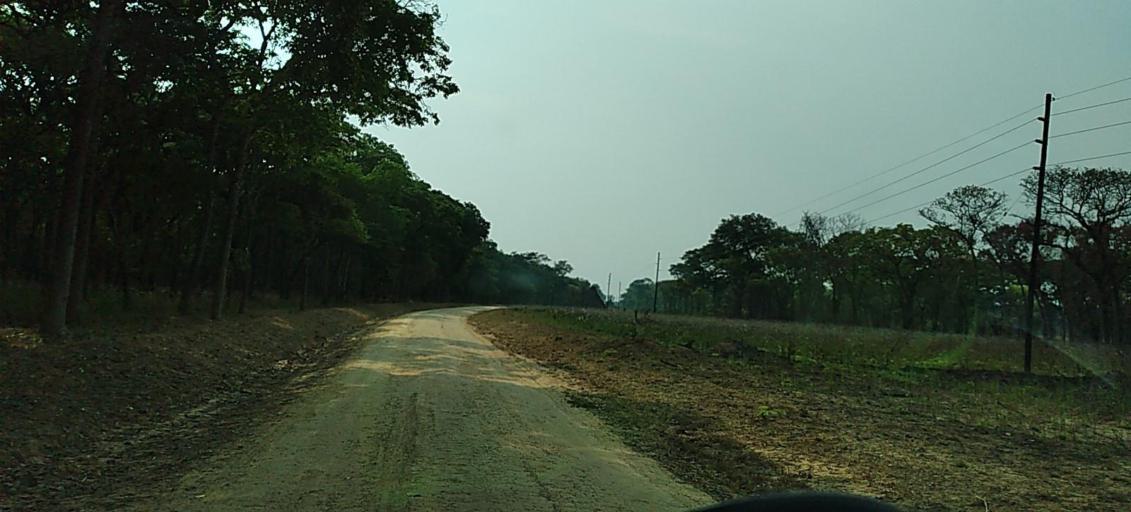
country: ZM
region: North-Western
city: Solwezi
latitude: -12.6943
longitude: 26.4042
